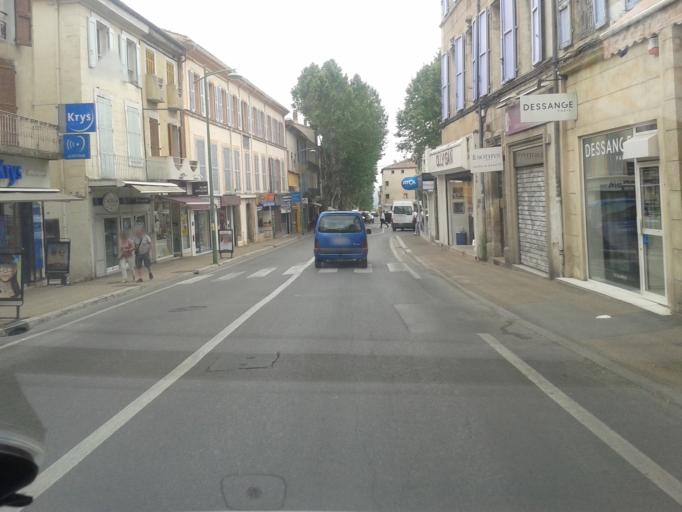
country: FR
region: Provence-Alpes-Cote d'Azur
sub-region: Departement des Alpes-de-Haute-Provence
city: Manosque
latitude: 43.8313
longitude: 5.7843
